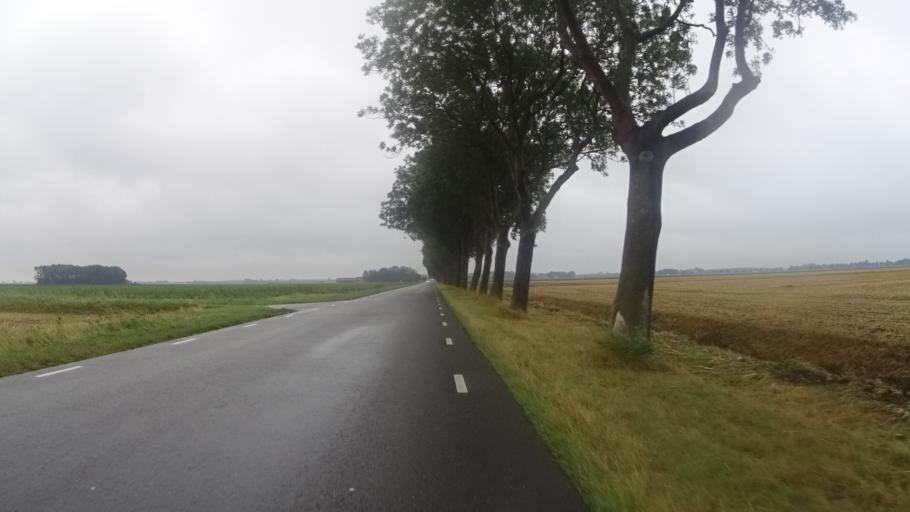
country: NL
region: Groningen
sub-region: Gemeente Veendam
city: Veendam
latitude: 53.1891
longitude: 6.9313
